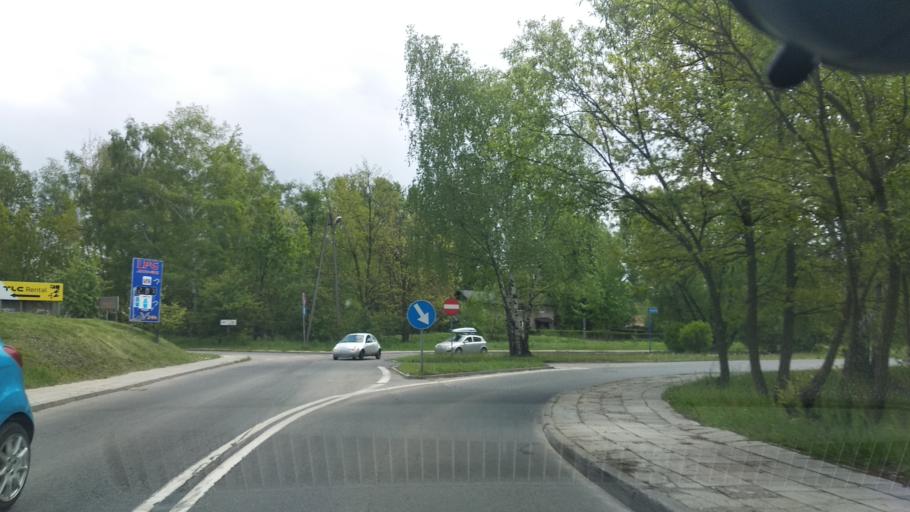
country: PL
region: Silesian Voivodeship
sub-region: Katowice
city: Katowice
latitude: 50.2456
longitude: 18.9816
